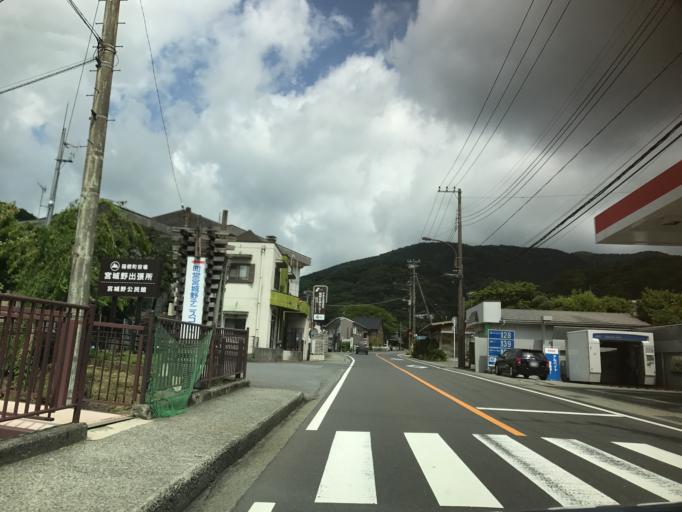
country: JP
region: Kanagawa
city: Hakone
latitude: 35.2539
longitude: 139.0504
